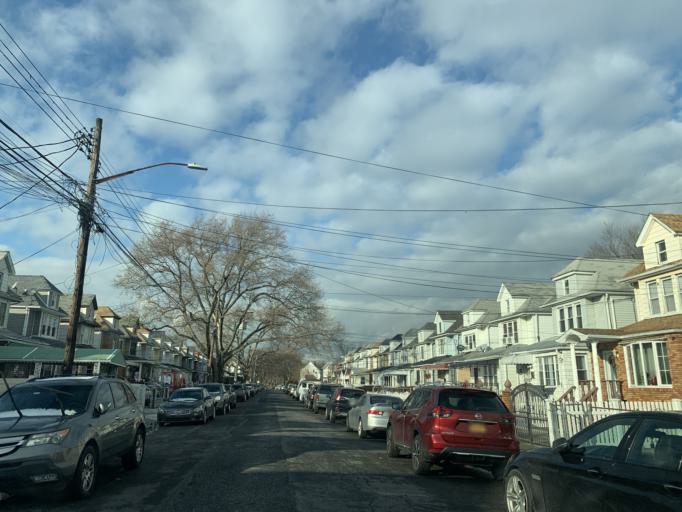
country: US
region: New York
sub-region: Queens County
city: Jamaica
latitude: 40.6843
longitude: -73.8100
